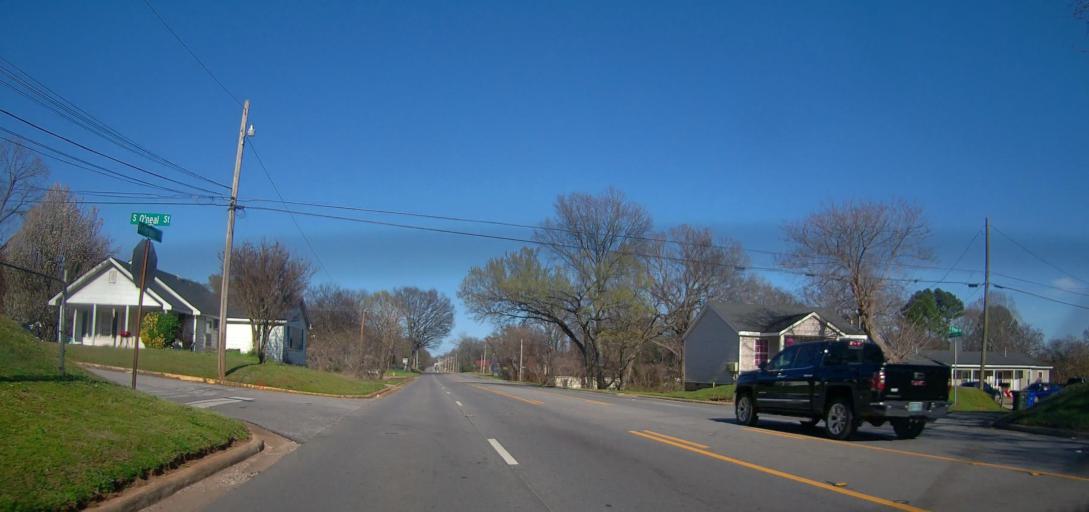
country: US
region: Alabama
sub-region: Lauderdale County
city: East Florence
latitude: 34.8074
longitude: -87.6416
